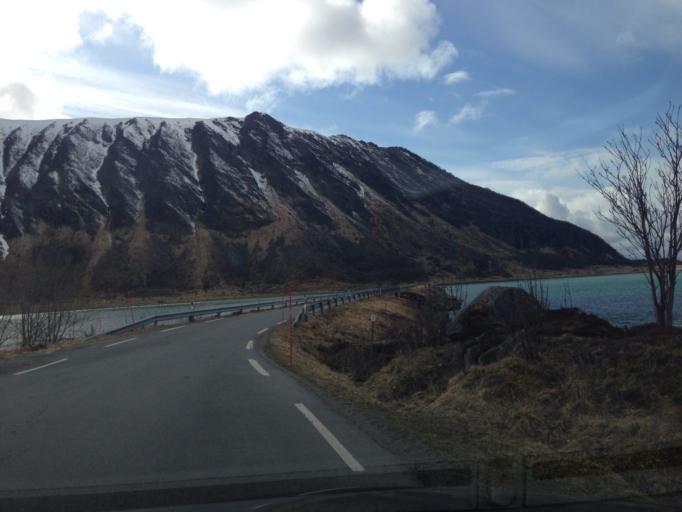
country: NO
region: Nordland
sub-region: Vagan
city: Svolvaer
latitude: 68.3944
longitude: 14.5585
